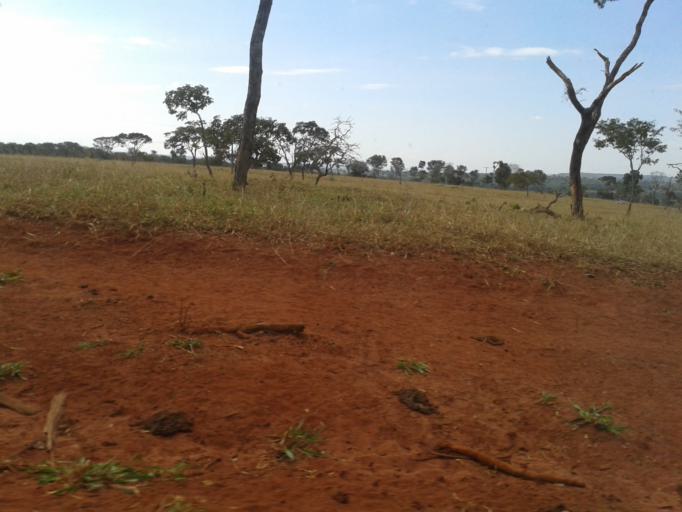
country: BR
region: Minas Gerais
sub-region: Ituiutaba
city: Ituiutaba
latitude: -19.0721
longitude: -49.3638
